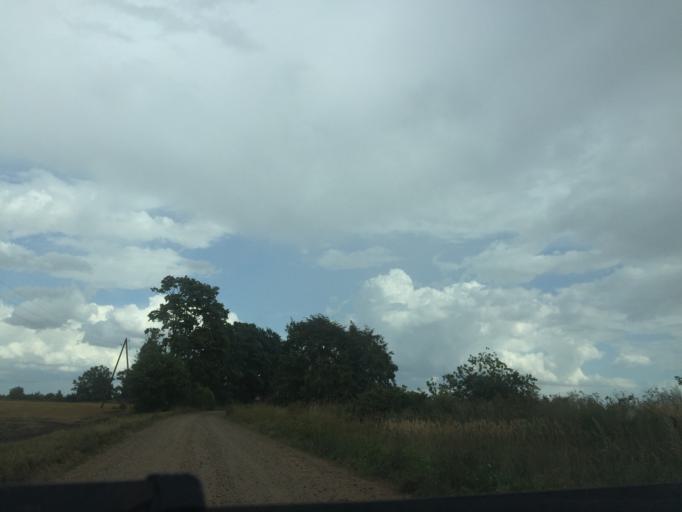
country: LV
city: Tervete
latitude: 56.3668
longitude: 23.4842
